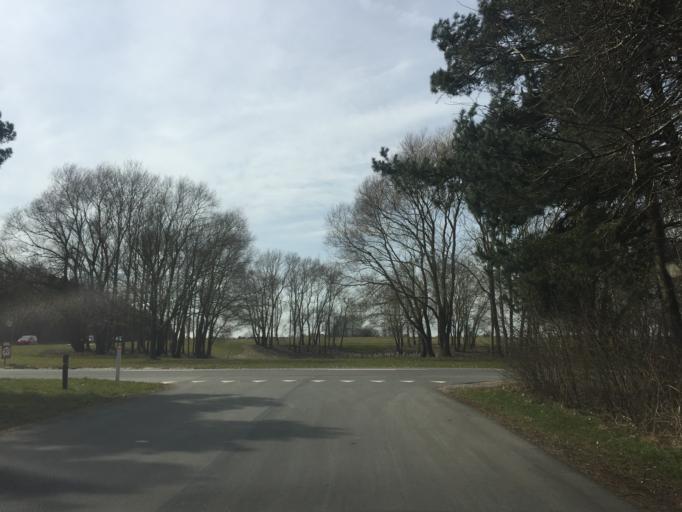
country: DK
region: Capital Region
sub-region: Hoje-Taastrup Kommune
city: Flong
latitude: 55.6659
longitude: 12.1810
